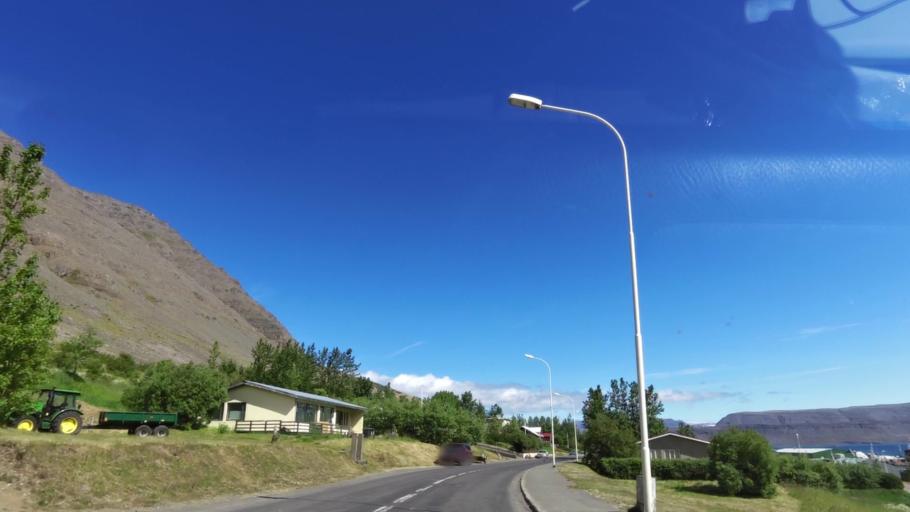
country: IS
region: Westfjords
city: Isafjoerdur
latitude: 65.6826
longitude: -23.6080
